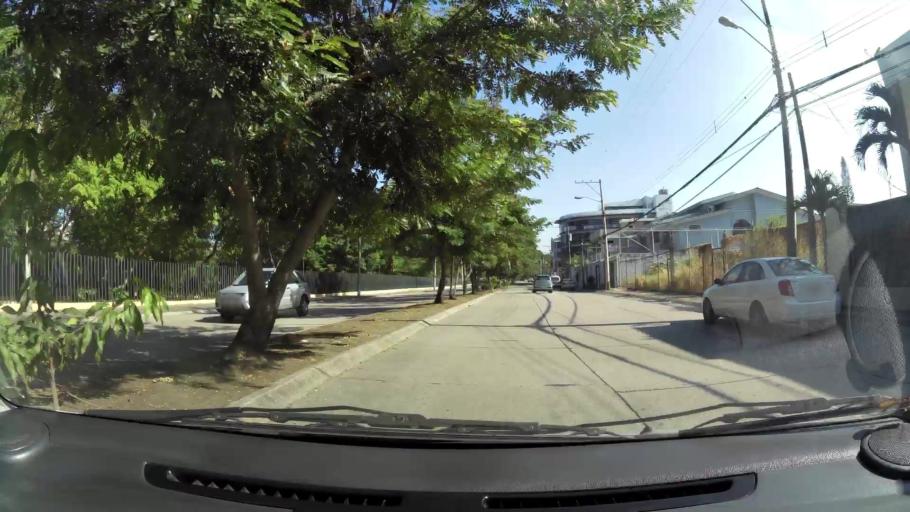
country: EC
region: Guayas
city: Guayaquil
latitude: -2.1645
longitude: -79.9002
